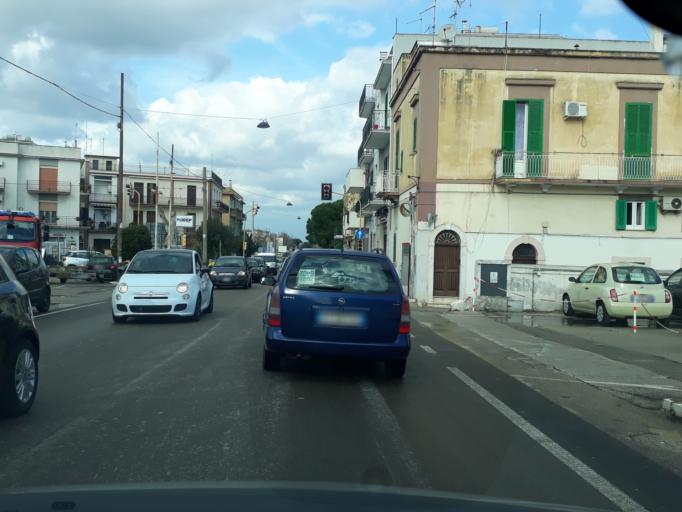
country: IT
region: Apulia
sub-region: Provincia di Brindisi
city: Fasano
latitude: 40.8390
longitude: 17.3598
